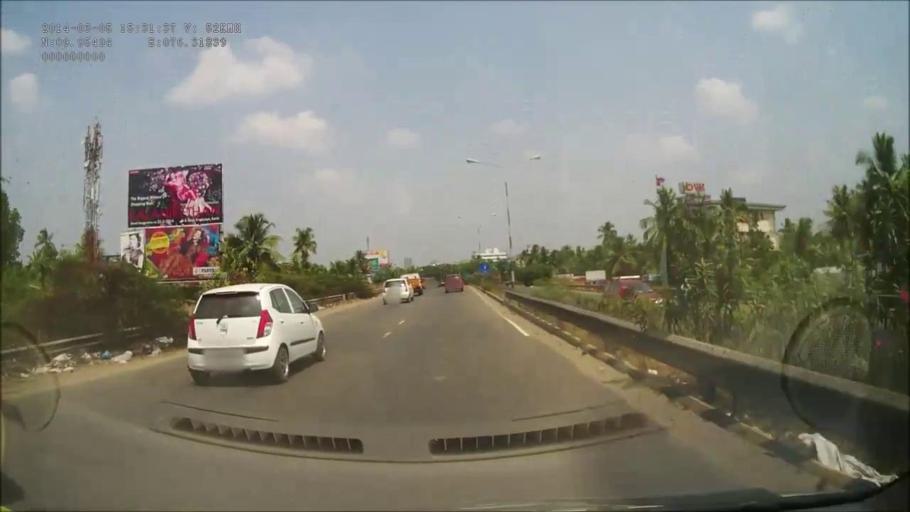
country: IN
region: Kerala
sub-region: Ernakulam
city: Cochin
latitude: 9.9552
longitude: 76.3184
